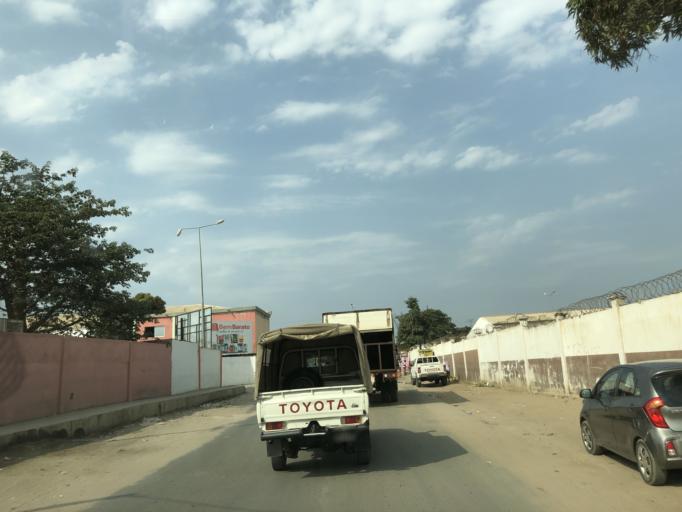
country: AO
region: Luanda
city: Luanda
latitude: -8.8932
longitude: 13.3535
